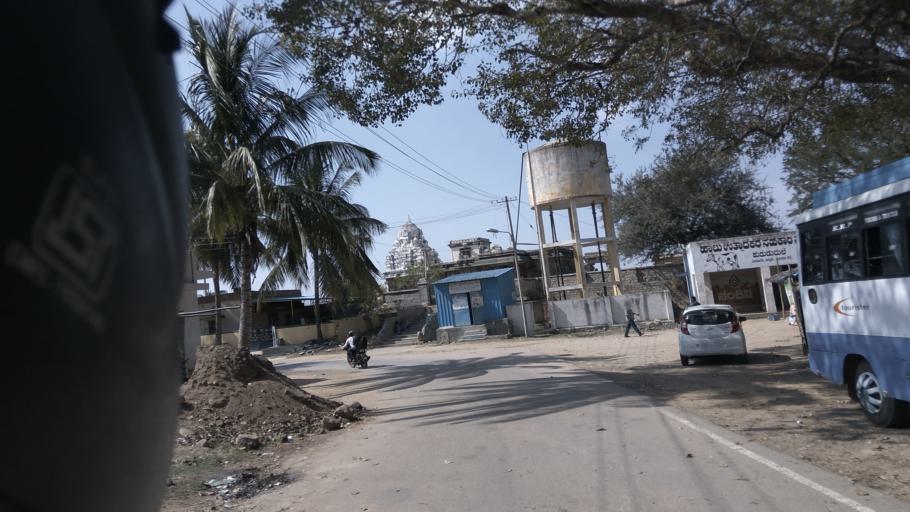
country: IN
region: Karnataka
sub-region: Kolar
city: Mulbagal
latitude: 13.2114
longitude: 78.3693
